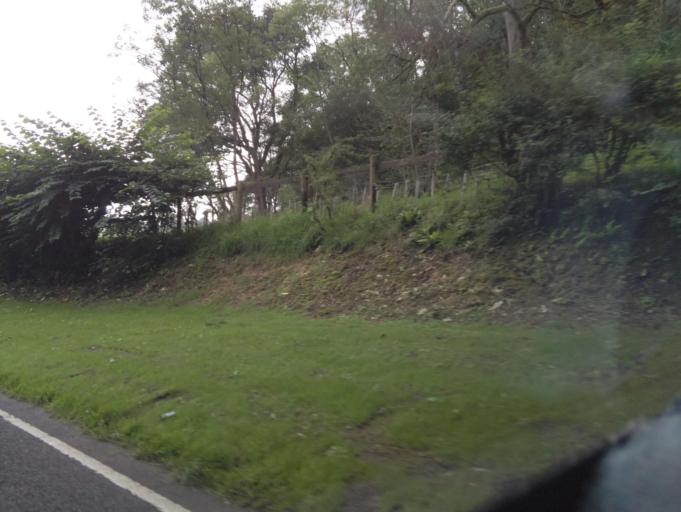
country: GB
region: England
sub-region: North Somerset
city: Easton-in-Gordano
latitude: 51.4554
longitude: -2.7154
